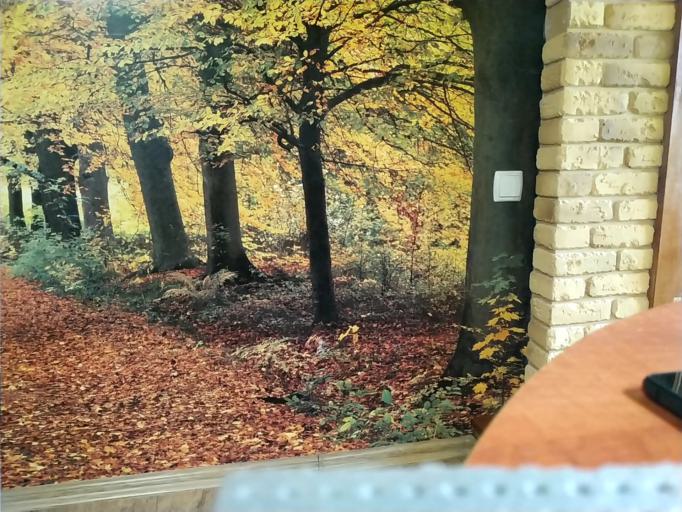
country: RU
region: Tverskaya
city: Likhoslavl'
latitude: 57.0170
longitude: 35.3812
